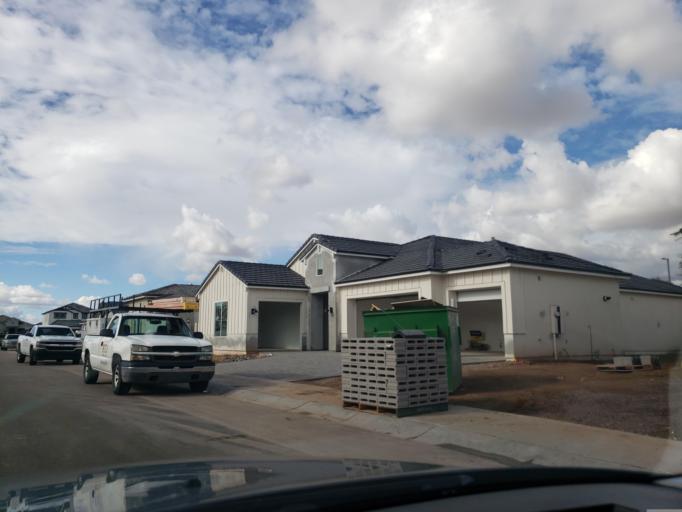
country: US
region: Arizona
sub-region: Maricopa County
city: Paradise Valley
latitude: 33.6473
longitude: -111.9694
